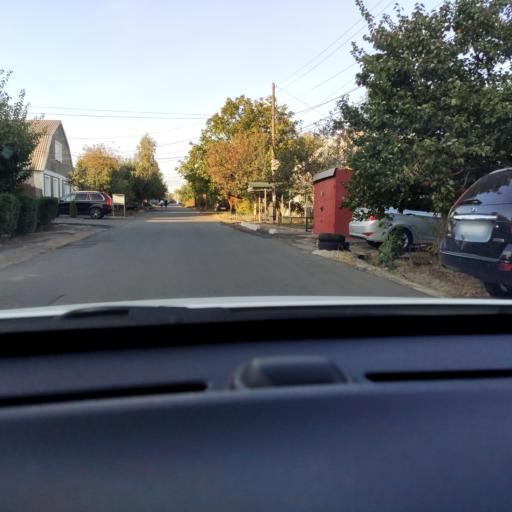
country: RU
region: Voronezj
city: Voronezh
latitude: 51.6924
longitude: 39.1504
